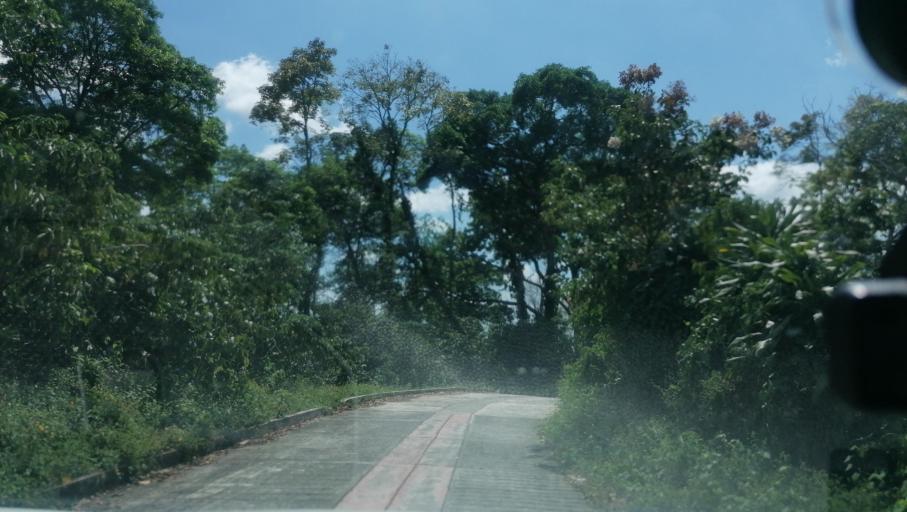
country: MX
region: Chiapas
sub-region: Cacahoatan
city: Benito Juarez
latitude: 15.0442
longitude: -92.1478
